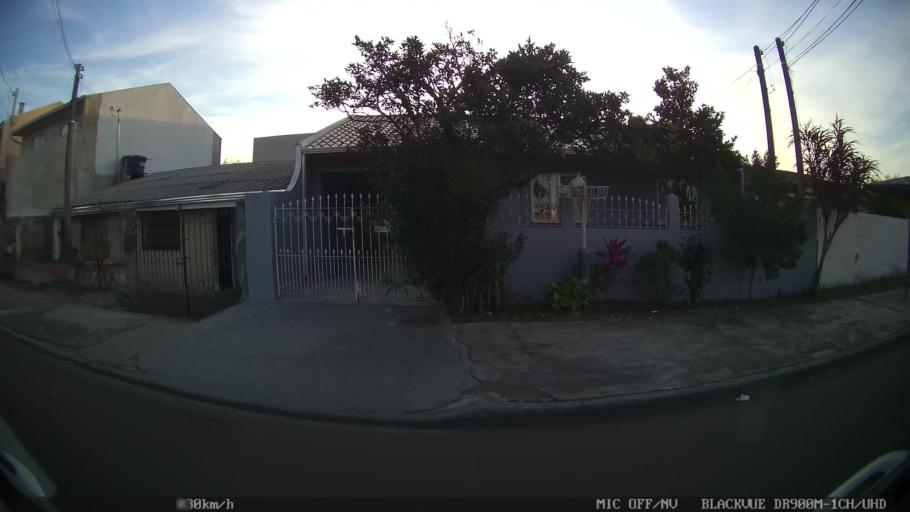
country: BR
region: Parana
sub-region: Pinhais
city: Pinhais
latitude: -25.4495
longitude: -49.1685
